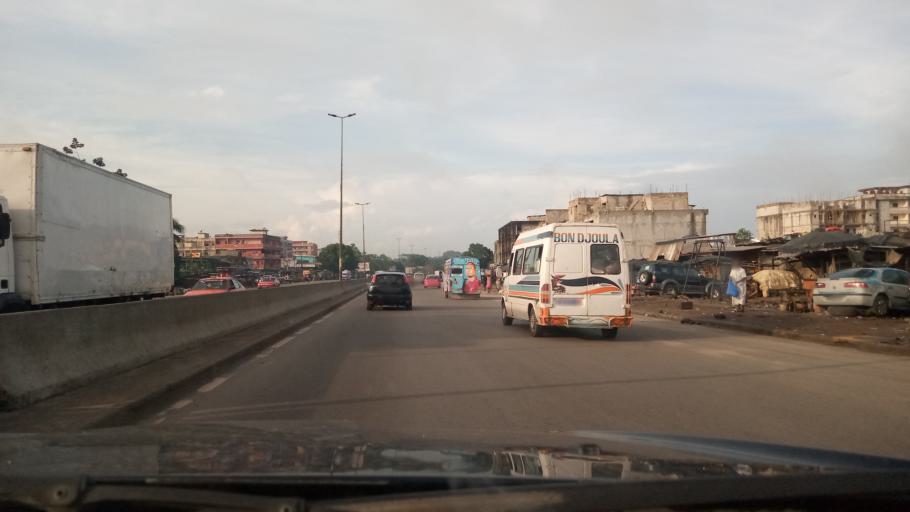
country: CI
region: Lagunes
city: Abobo
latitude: 5.4107
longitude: -4.0161
